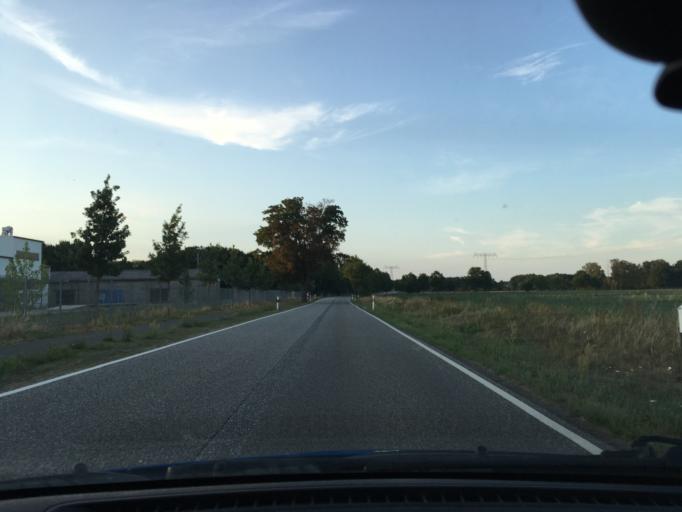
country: DE
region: Mecklenburg-Vorpommern
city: Boizenburg
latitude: 53.3835
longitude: 10.7498
